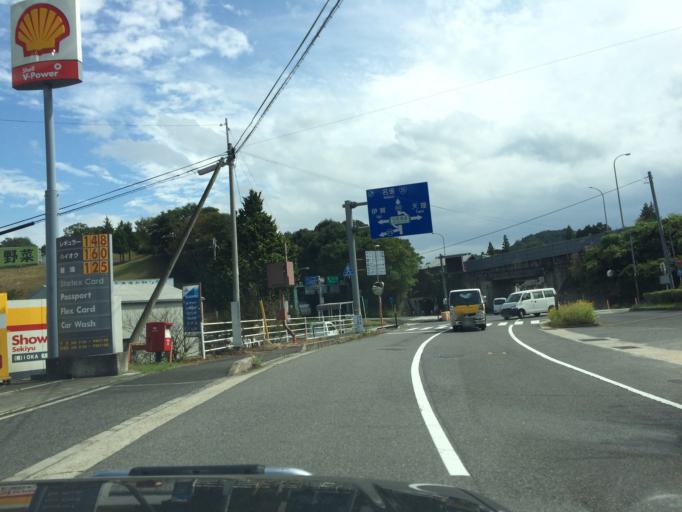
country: JP
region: Mie
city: Nabari
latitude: 34.6814
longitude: 136.0387
